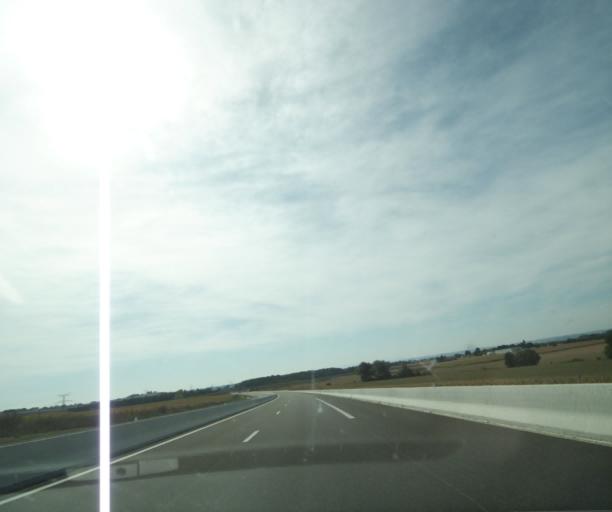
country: FR
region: Auvergne
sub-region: Departement de l'Allier
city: Vendat
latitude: 46.1331
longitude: 3.3018
